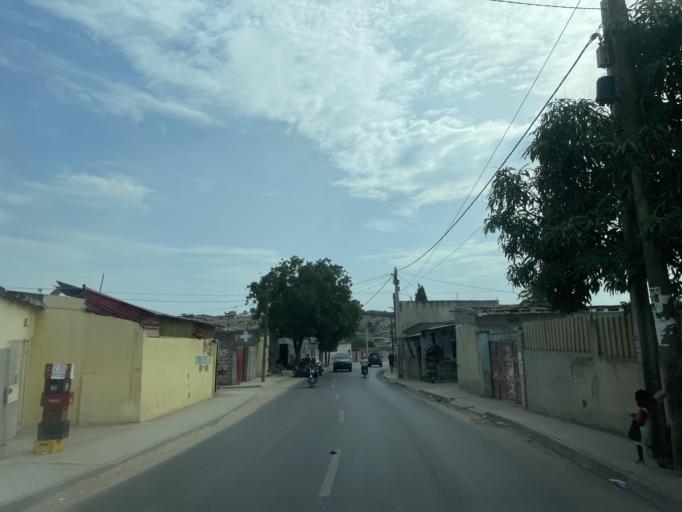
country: AO
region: Luanda
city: Luanda
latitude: -8.9342
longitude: 13.1988
